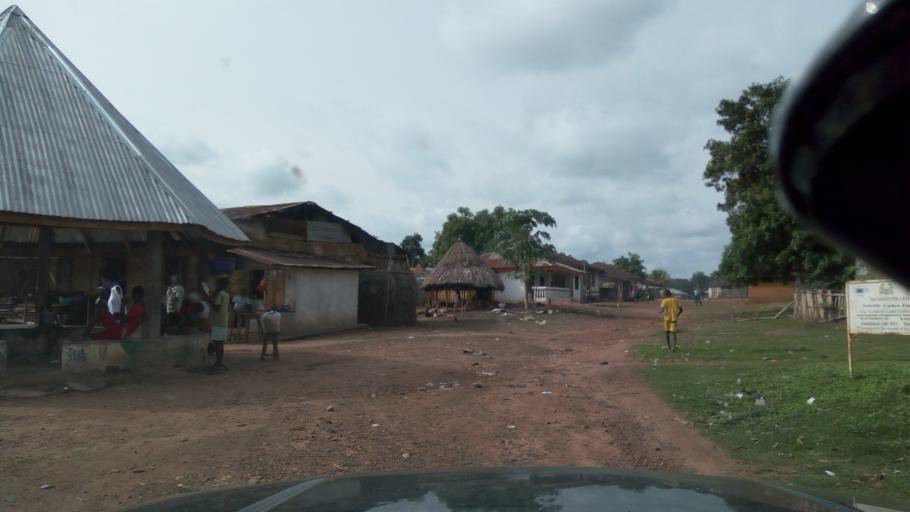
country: SL
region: Northern Province
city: Port Loko
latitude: 8.8034
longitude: -12.6381
